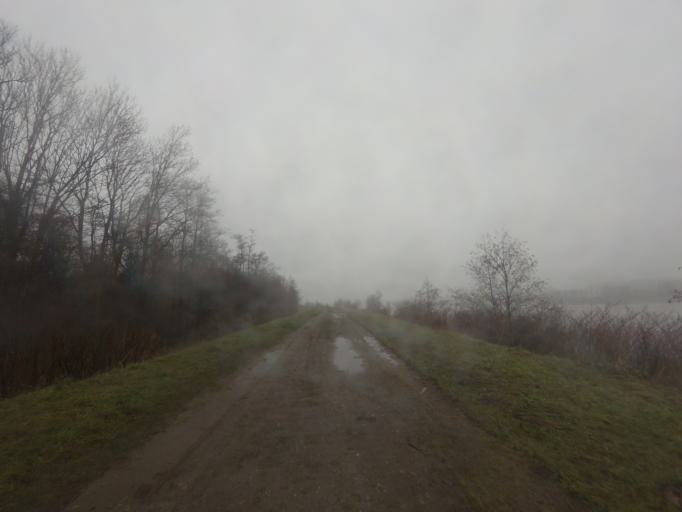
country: BE
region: Flanders
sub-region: Provincie Antwerpen
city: Hoboken
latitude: 51.1896
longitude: 4.3358
